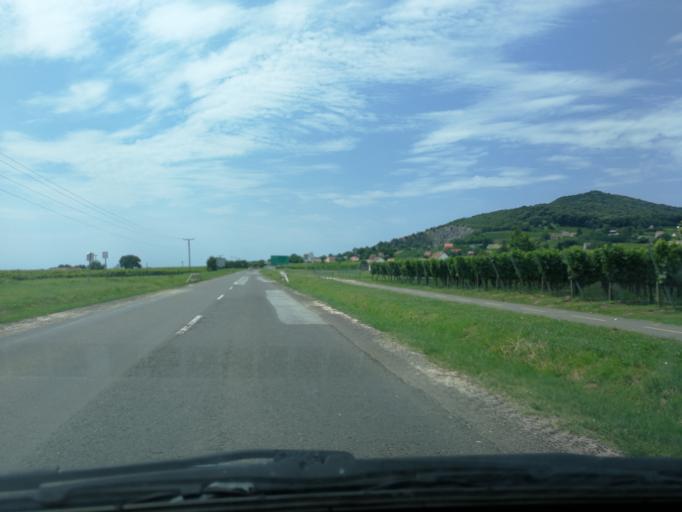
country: HU
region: Baranya
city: Villany
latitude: 45.8598
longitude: 18.4399
